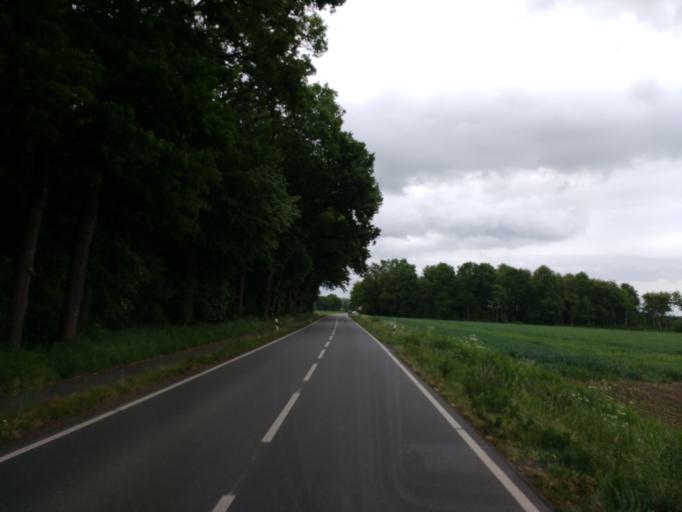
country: DE
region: Lower Saxony
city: Dinklage
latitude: 52.6351
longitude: 8.1603
